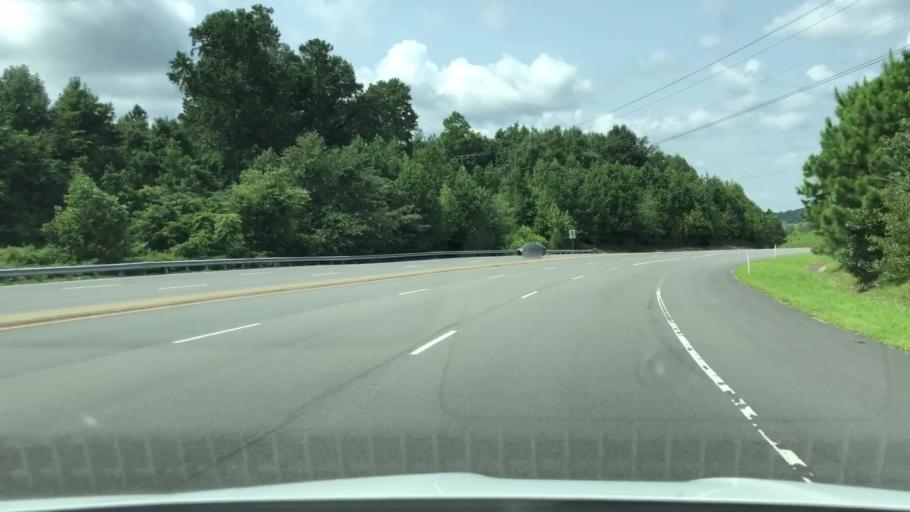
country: US
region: Virginia
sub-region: Henrico County
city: Chamberlayne
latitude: 37.6885
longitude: -77.4440
